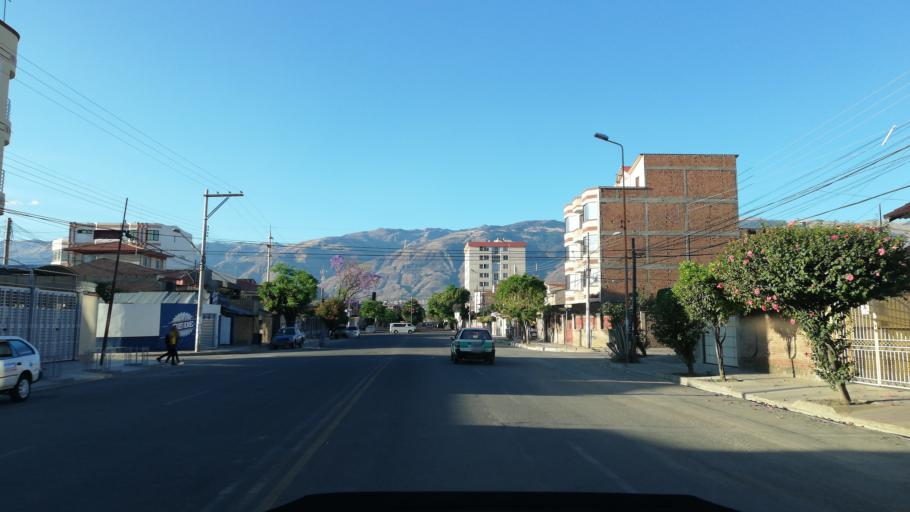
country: BO
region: Cochabamba
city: Cochabamba
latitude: -17.3976
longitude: -66.1741
